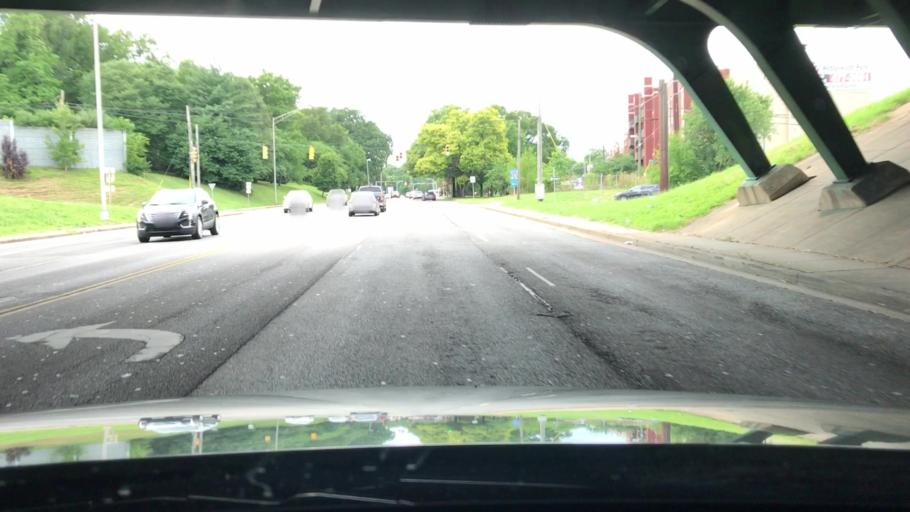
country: US
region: Tennessee
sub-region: Davidson County
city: Nashville
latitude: 36.1306
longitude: -86.7814
